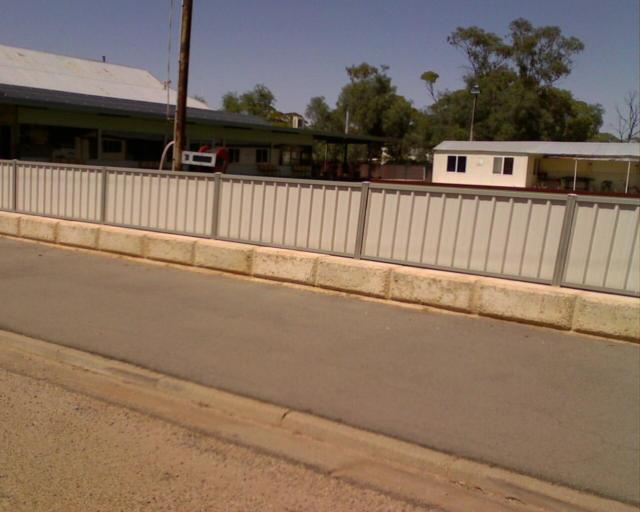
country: AU
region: Western Australia
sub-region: Merredin
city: Merredin
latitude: -31.6079
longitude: 117.8760
